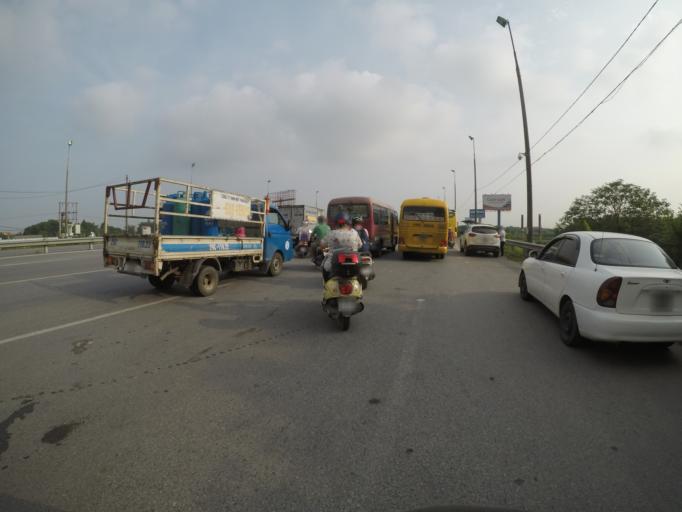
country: VN
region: Ha Noi
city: Me Linh
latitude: 21.2030
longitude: 105.7797
